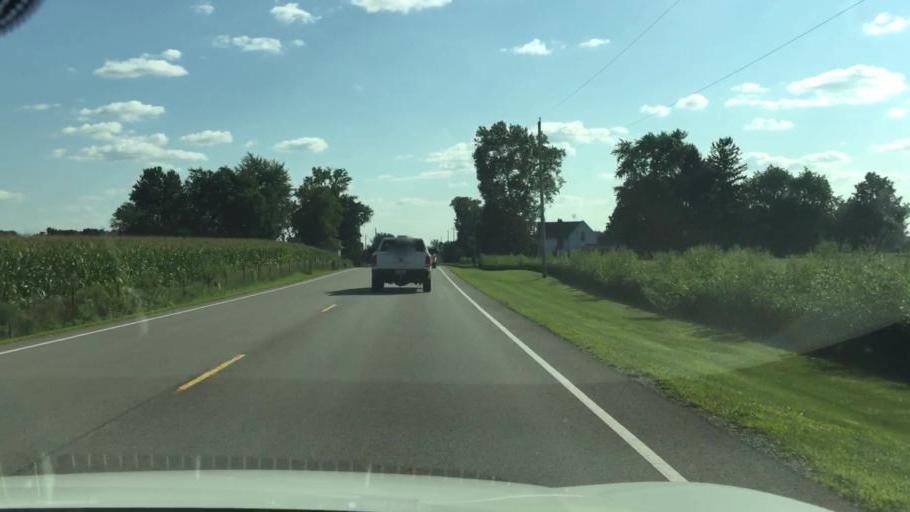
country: US
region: Ohio
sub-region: Champaign County
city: Mechanicsburg
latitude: 40.1282
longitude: -83.4881
